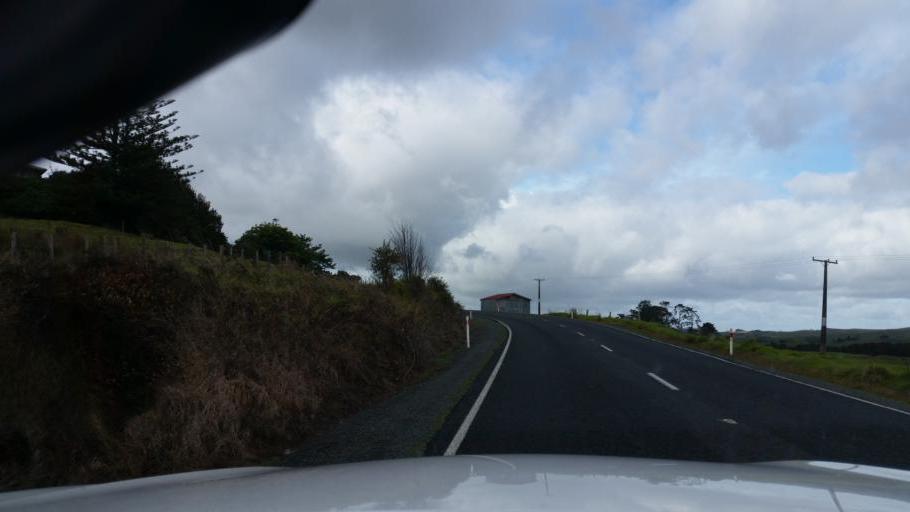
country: NZ
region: Northland
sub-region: Whangarei
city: Ruakaka
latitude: -35.9512
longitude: 174.2933
